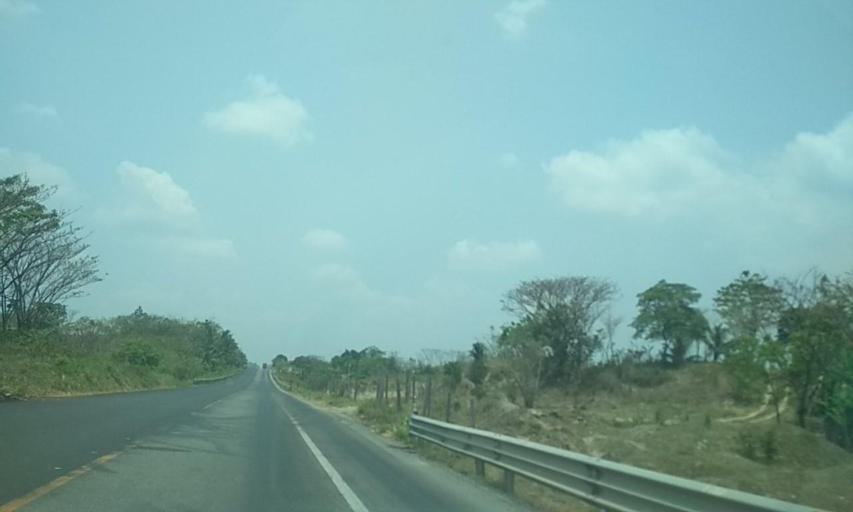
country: MX
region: Tabasco
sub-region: Huimanguillo
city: Francisco Rueda
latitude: 17.7141
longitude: -93.9451
